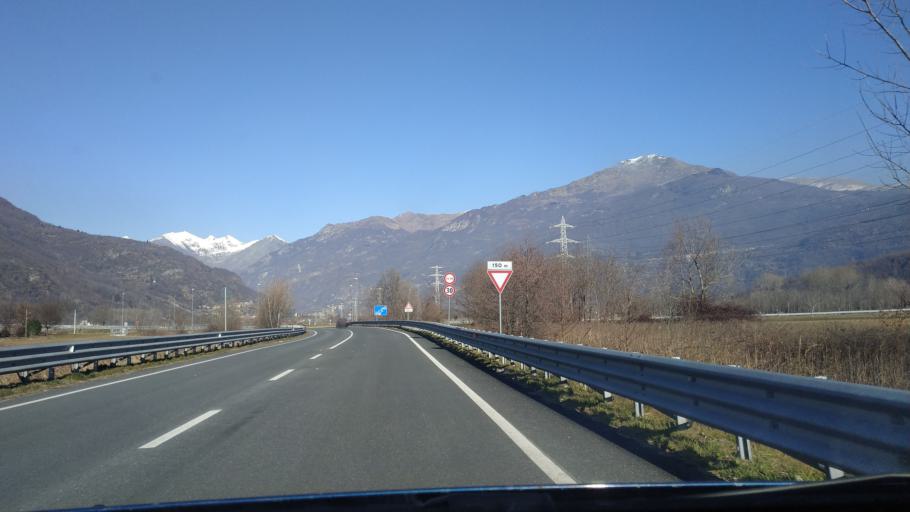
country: IT
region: Piedmont
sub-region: Provincia di Torino
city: Quassolo
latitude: 45.5063
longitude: 7.8356
